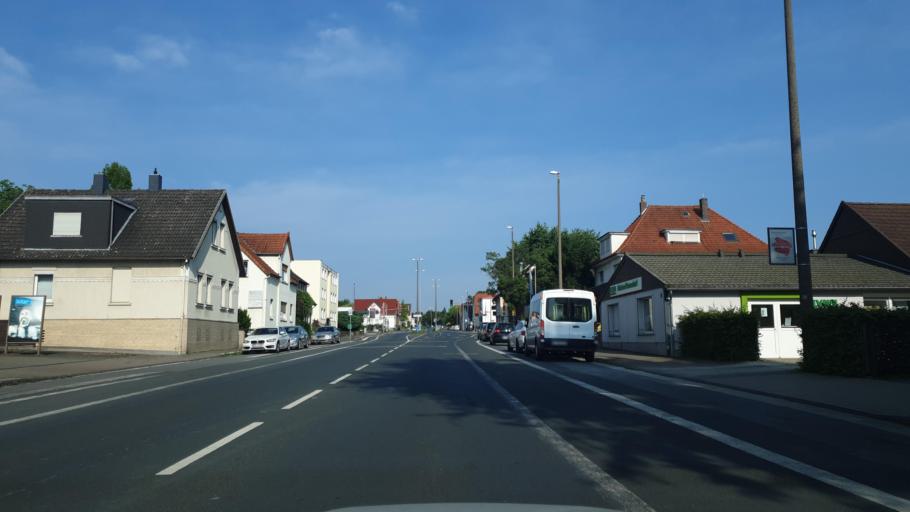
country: DE
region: North Rhine-Westphalia
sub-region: Regierungsbezirk Detmold
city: Herford
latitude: 52.1209
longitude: 8.6508
